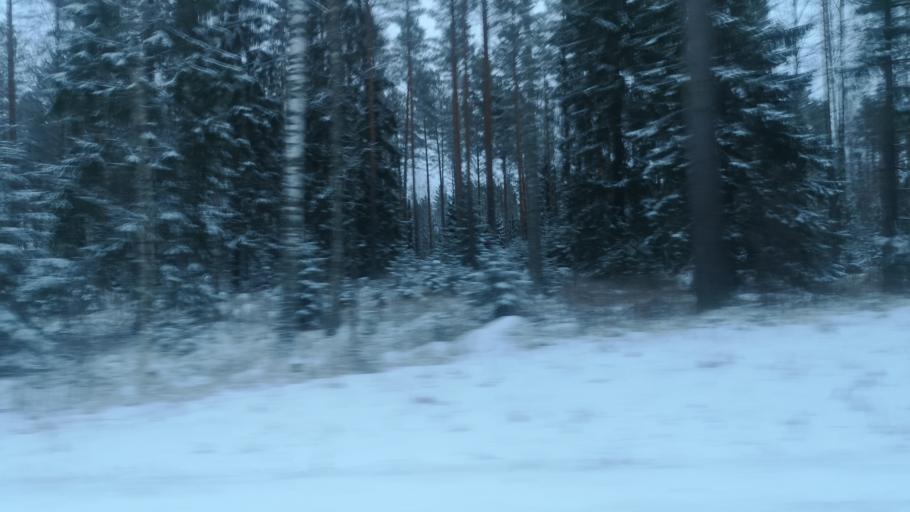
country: FI
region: Southern Savonia
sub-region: Savonlinna
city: Savonlinna
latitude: 62.0175
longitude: 28.7283
